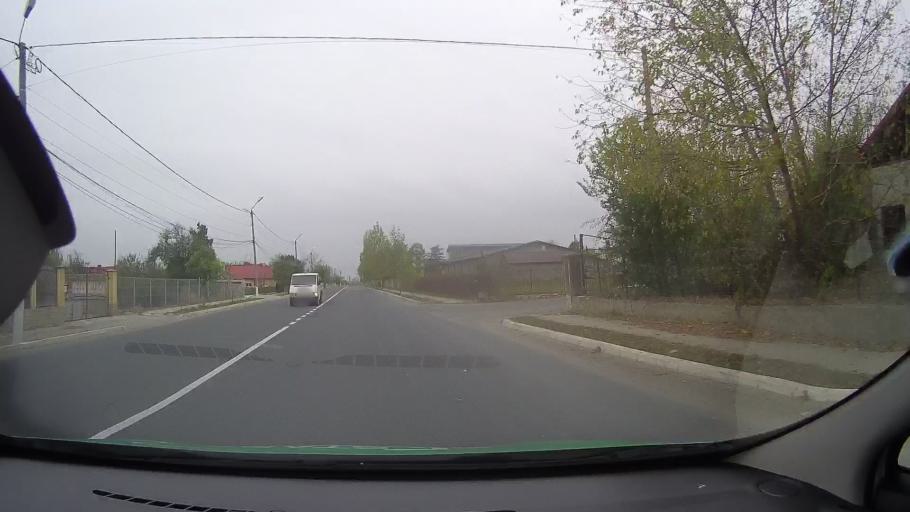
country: RO
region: Constanta
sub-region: Oras Harsova
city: Harsova
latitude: 44.6900
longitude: 27.9593
